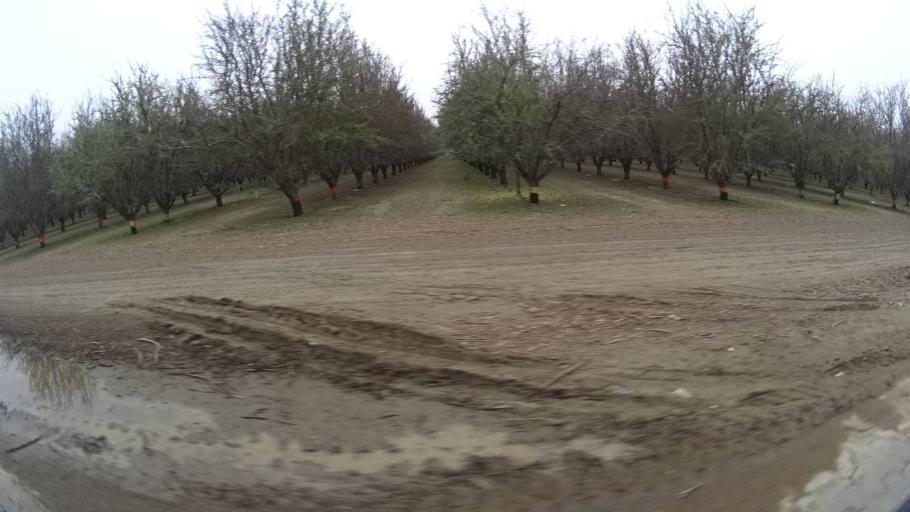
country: US
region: California
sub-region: Kern County
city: Buttonwillow
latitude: 35.5720
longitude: -119.5193
